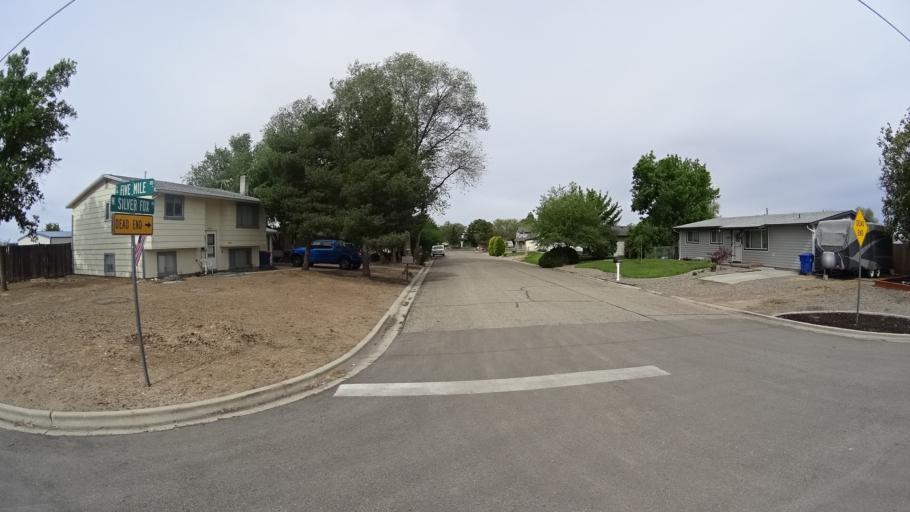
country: US
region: Idaho
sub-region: Ada County
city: Kuna
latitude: 43.5291
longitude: -116.3146
